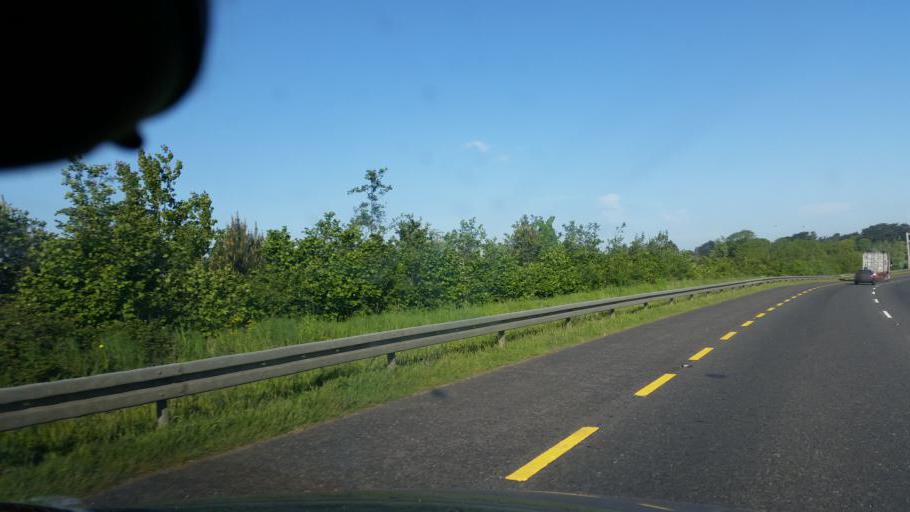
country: IE
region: Leinster
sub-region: Dublin City
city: Finglas
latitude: 53.4200
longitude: -6.3246
